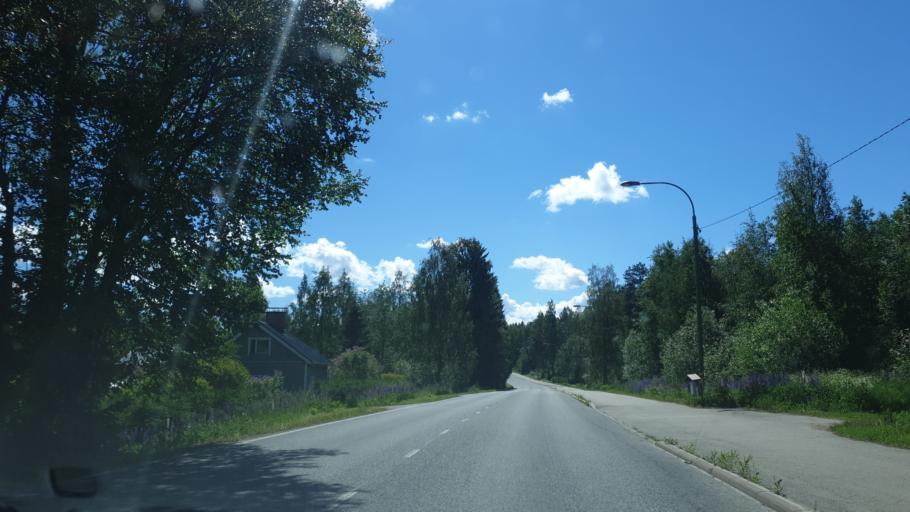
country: FI
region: Northern Savo
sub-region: Koillis-Savo
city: Kaavi
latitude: 62.9812
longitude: 28.4987
